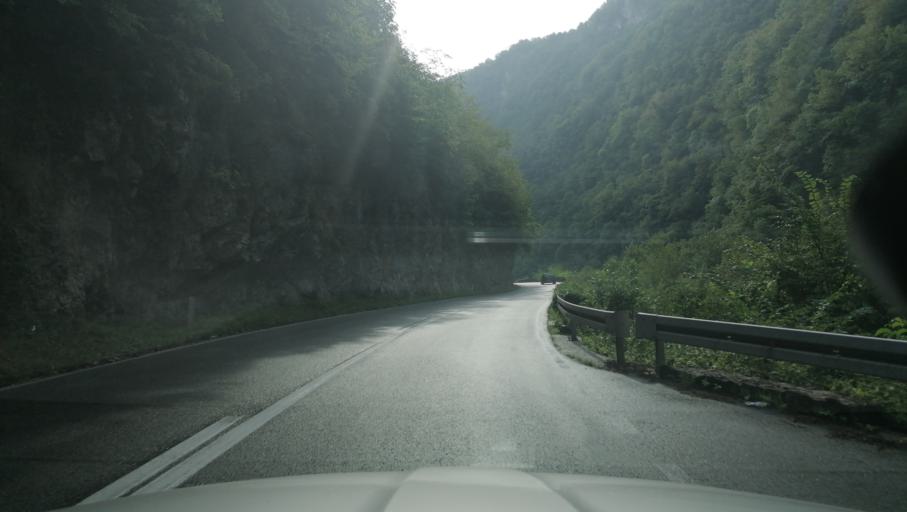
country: BA
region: Republika Srpska
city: Starcevica
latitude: 44.6873
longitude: 17.1890
